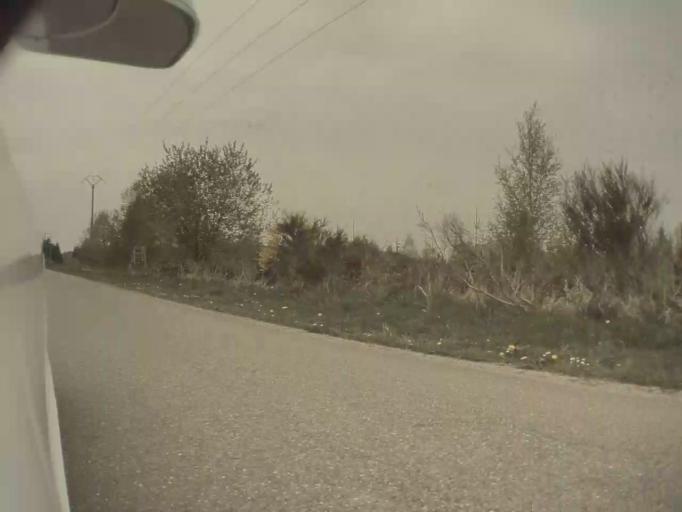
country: BE
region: Wallonia
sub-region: Province du Luxembourg
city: La Roche-en-Ardenne
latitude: 50.2270
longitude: 5.6030
